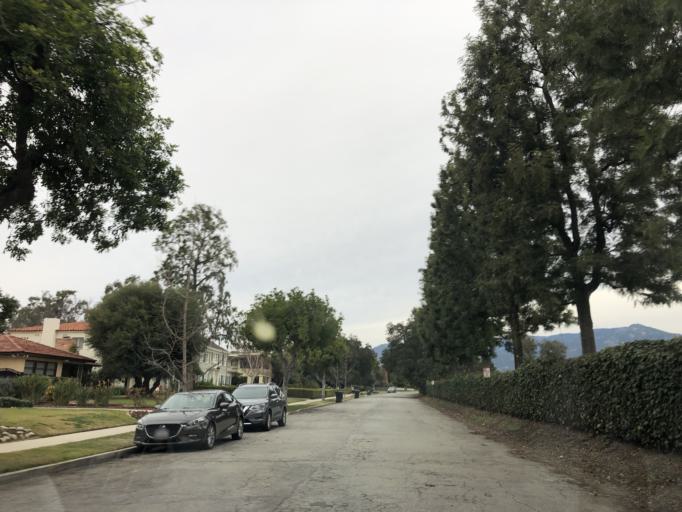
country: US
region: California
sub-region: Los Angeles County
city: San Gabriel
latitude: 34.1040
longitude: -118.0966
